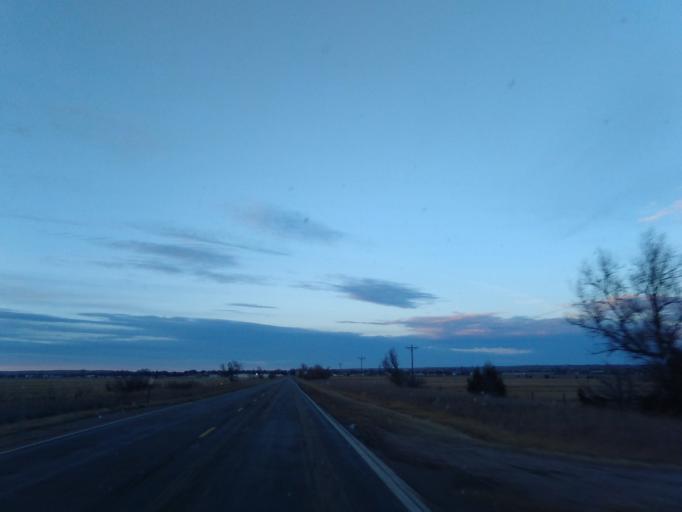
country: US
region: Nebraska
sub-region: Garden County
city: Oshkosh
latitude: 41.3865
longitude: -102.3476
